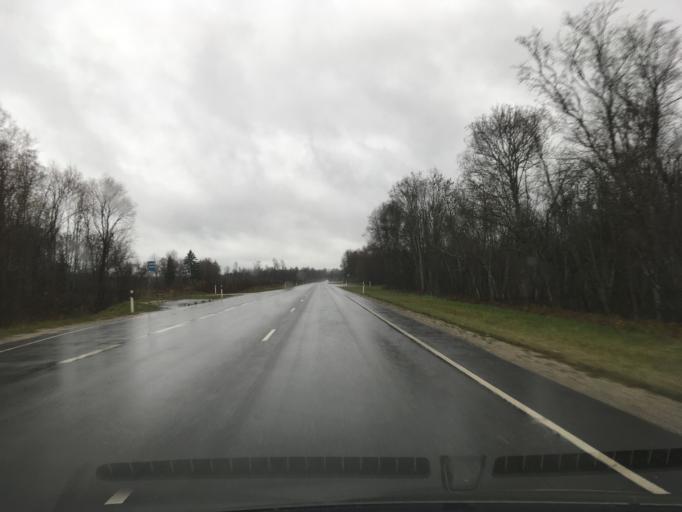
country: EE
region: Laeaene
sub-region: Lihula vald
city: Lihula
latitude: 58.8018
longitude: 24.0476
